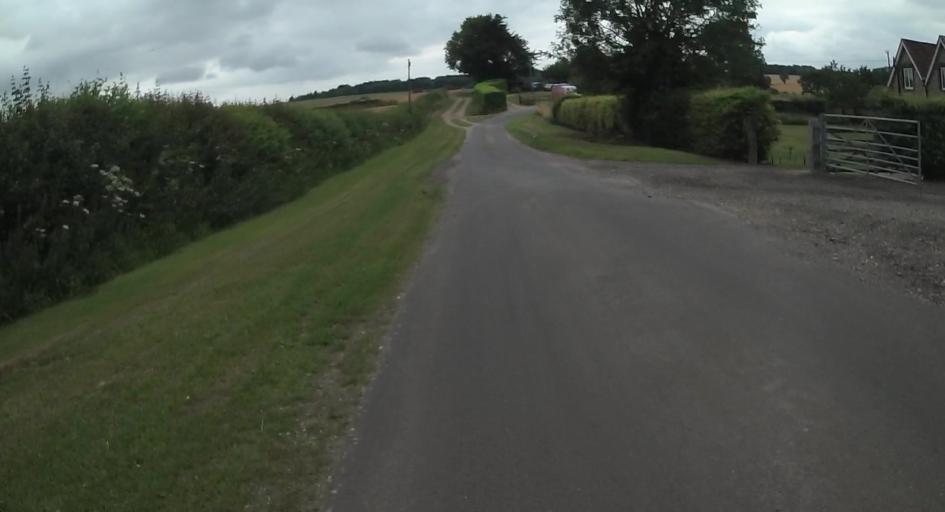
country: GB
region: England
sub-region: Hampshire
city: Swanmore
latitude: 51.0240
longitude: -1.1705
